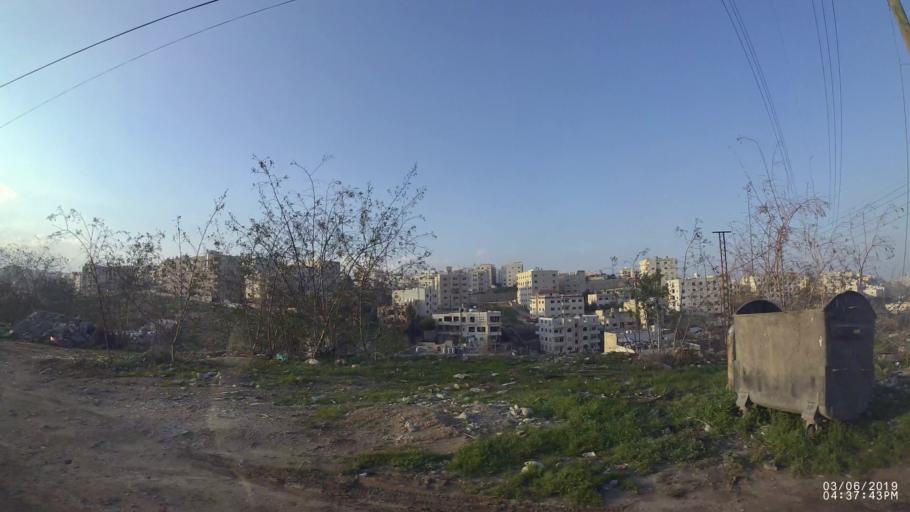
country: JO
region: Amman
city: Amman
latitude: 31.9860
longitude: 35.9697
